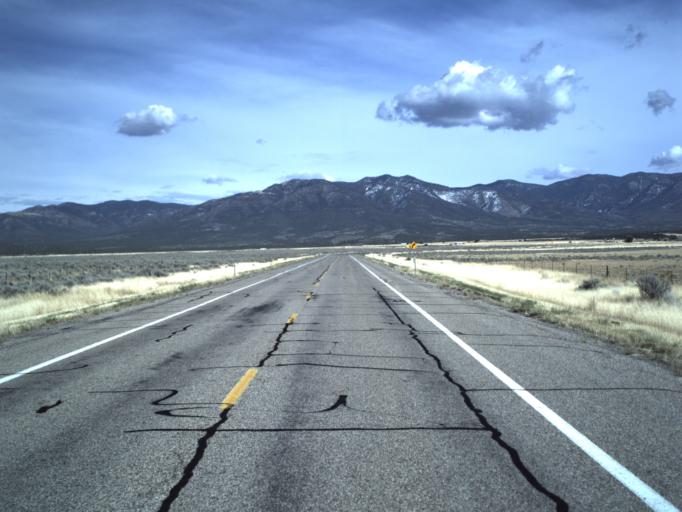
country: US
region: Utah
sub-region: Millard County
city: Fillmore
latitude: 39.1143
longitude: -112.2842
